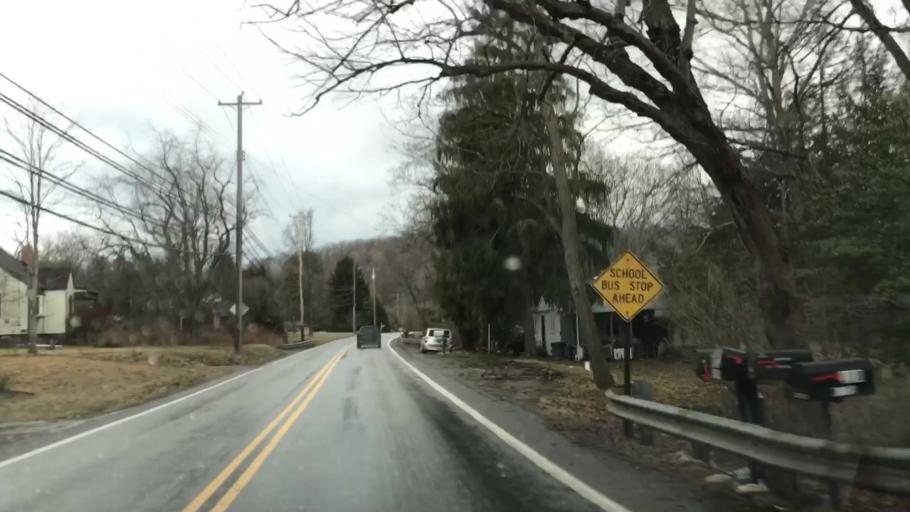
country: US
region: Pennsylvania
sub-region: Allegheny County
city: Bell Acres
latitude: 40.6077
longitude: -80.1749
